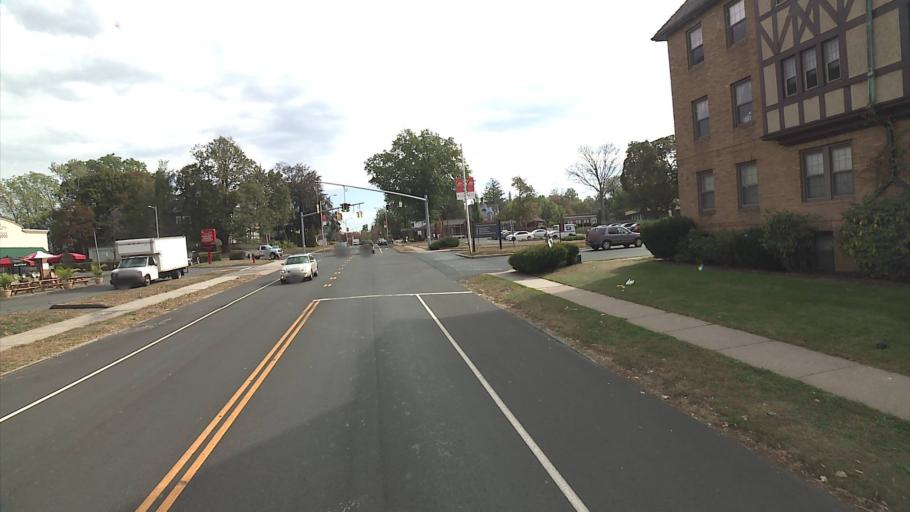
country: US
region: Connecticut
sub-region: Hartford County
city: New Britain
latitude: 41.6654
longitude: -72.7936
